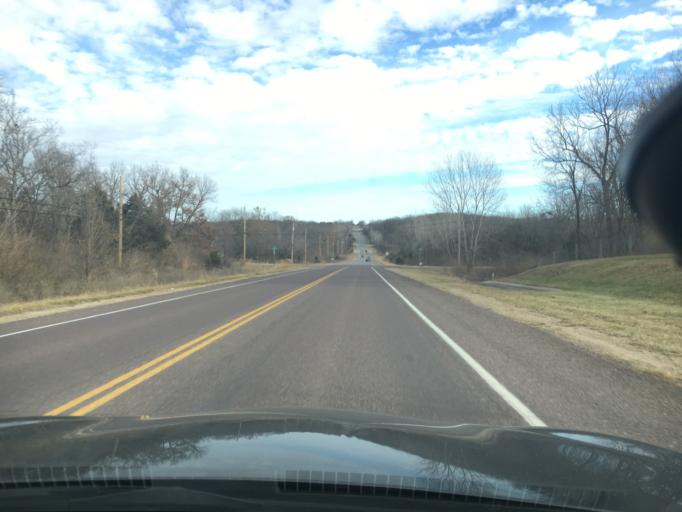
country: US
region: Kansas
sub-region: Johnson County
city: Spring Hill
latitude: 38.8036
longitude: -94.6878
